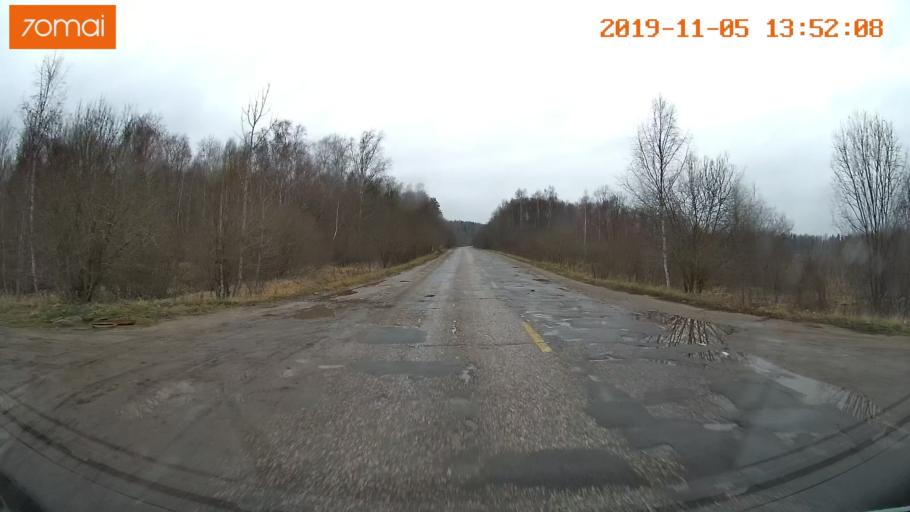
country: RU
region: Ivanovo
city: Kaminskiy
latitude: 57.0267
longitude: 41.3907
